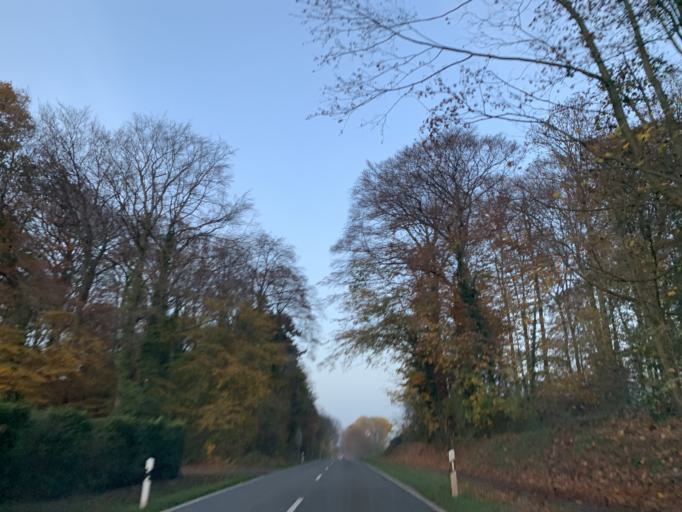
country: DE
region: North Rhine-Westphalia
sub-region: Regierungsbezirk Munster
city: Nottuln
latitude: 51.9752
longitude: 7.3481
